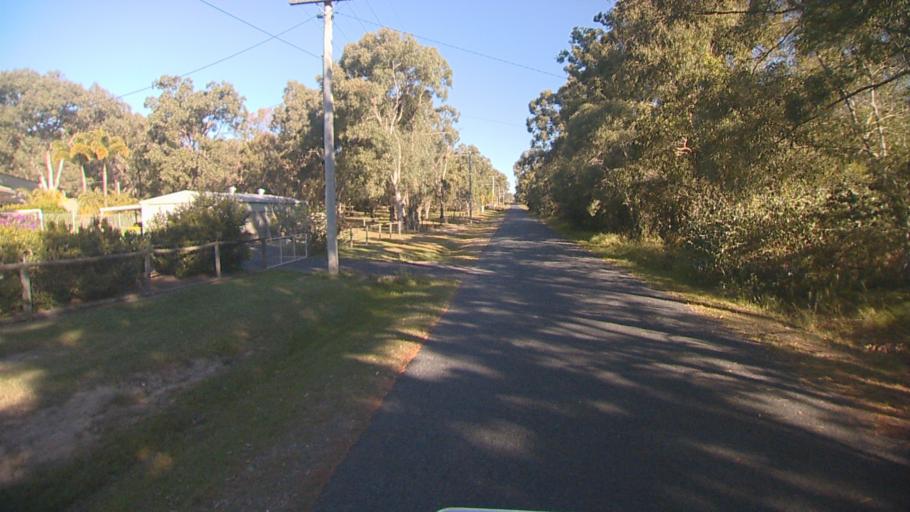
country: AU
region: Queensland
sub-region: Logan
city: Logan Reserve
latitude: -27.7135
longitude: 153.1075
